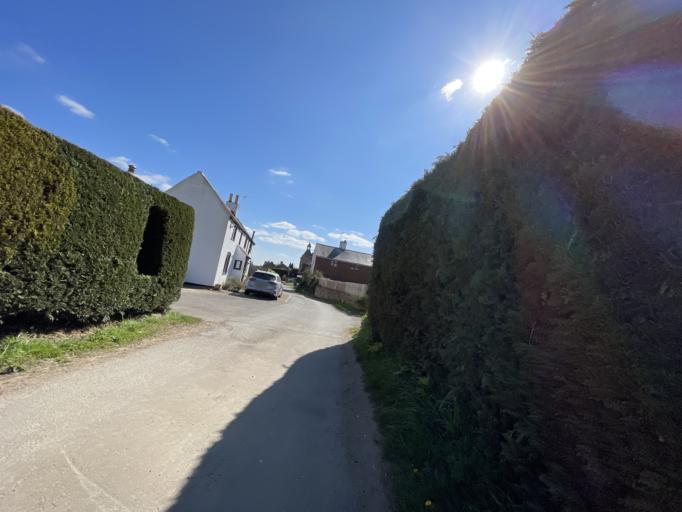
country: GB
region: England
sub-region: Warwickshire
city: Dunchurch
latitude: 52.3353
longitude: -1.3126
